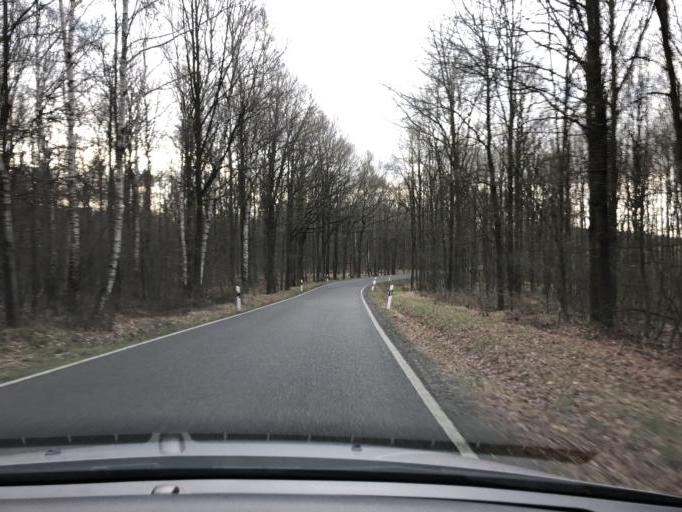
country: DE
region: Saxony
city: Grossbothen
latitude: 51.2033
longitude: 12.7888
